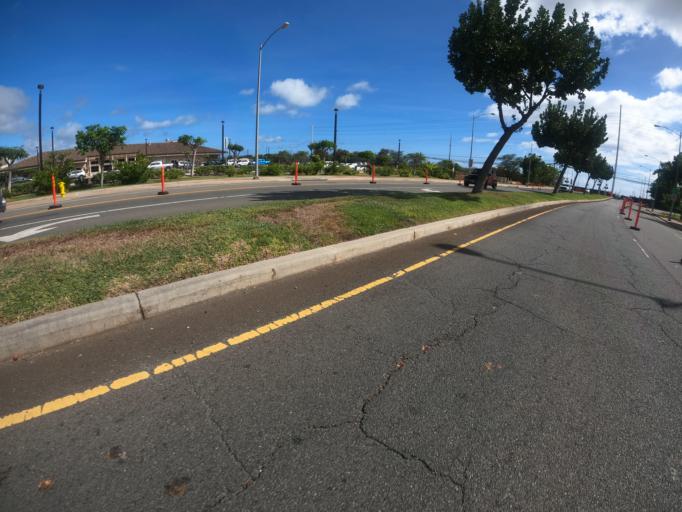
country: US
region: Hawaii
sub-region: Honolulu County
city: Makakilo City
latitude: 21.3275
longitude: -158.0865
